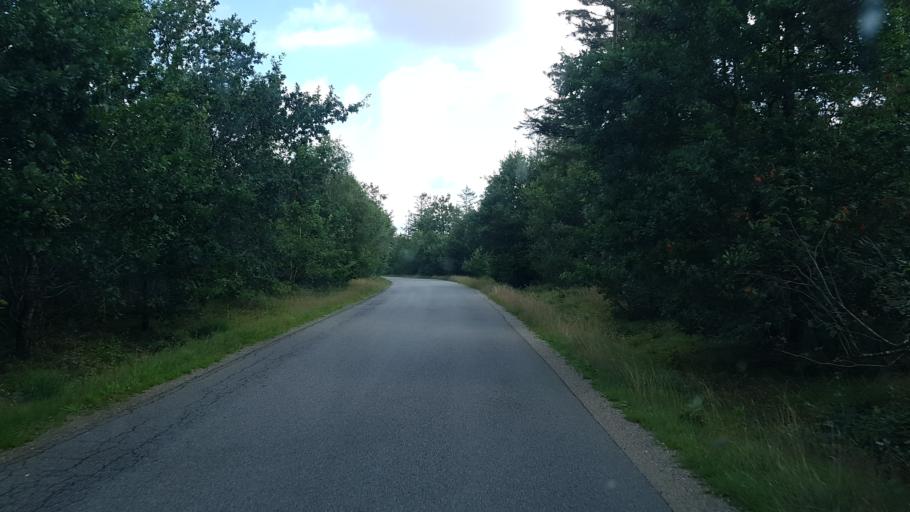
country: DK
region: South Denmark
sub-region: Varde Kommune
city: Olgod
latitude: 55.7903
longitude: 8.7356
